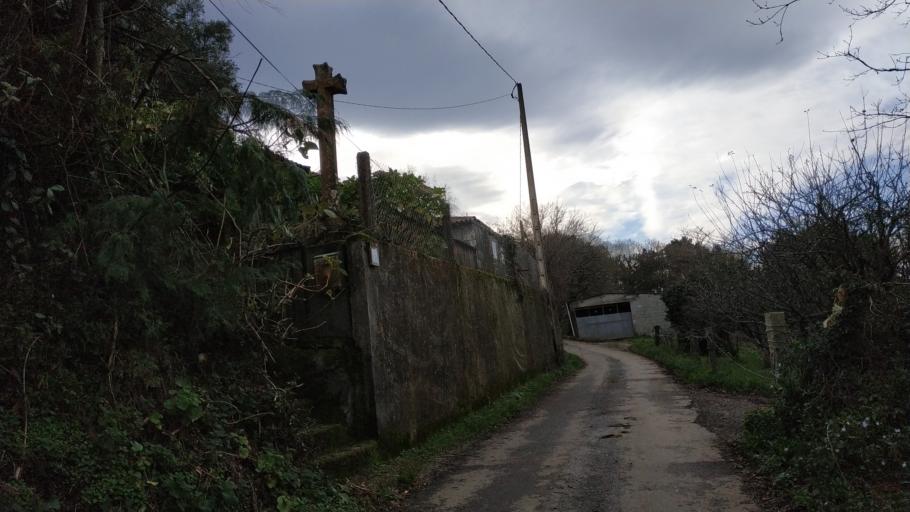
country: ES
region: Galicia
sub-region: Provincia de Pontevedra
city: Silleda
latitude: 42.7766
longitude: -8.1705
